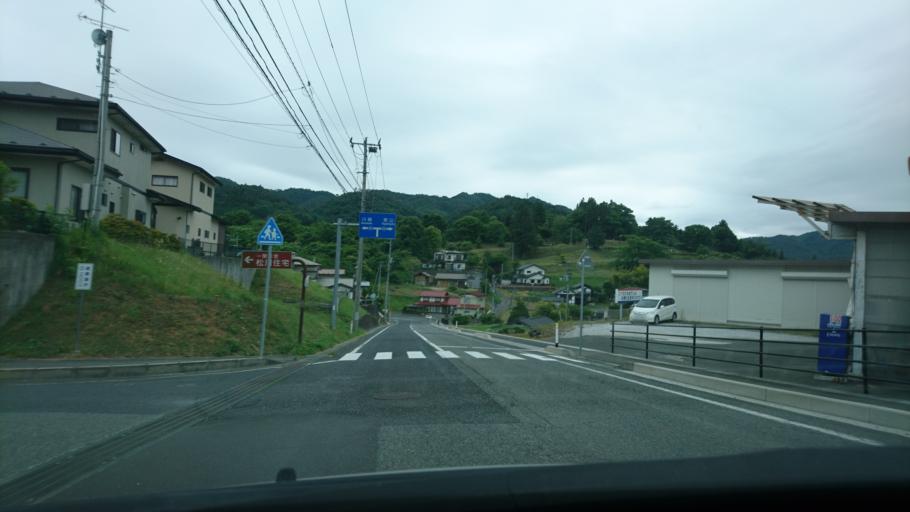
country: JP
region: Iwate
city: Ichinoseki
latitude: 38.9526
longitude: 141.2557
